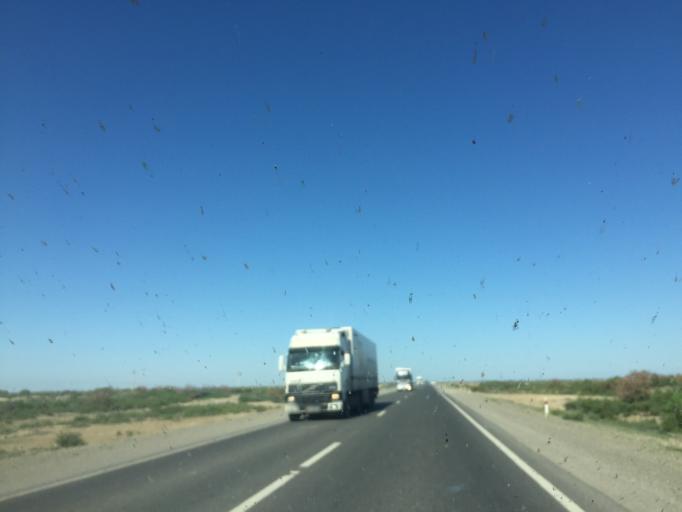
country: KZ
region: Qyzylorda
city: Terenozek
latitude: 44.8630
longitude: 64.8496
